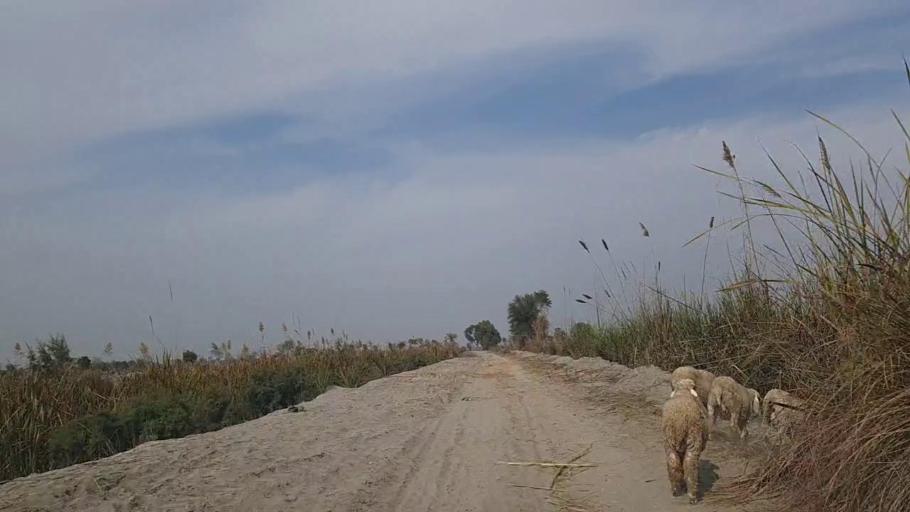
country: PK
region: Sindh
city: Daur
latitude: 26.4626
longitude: 68.4072
